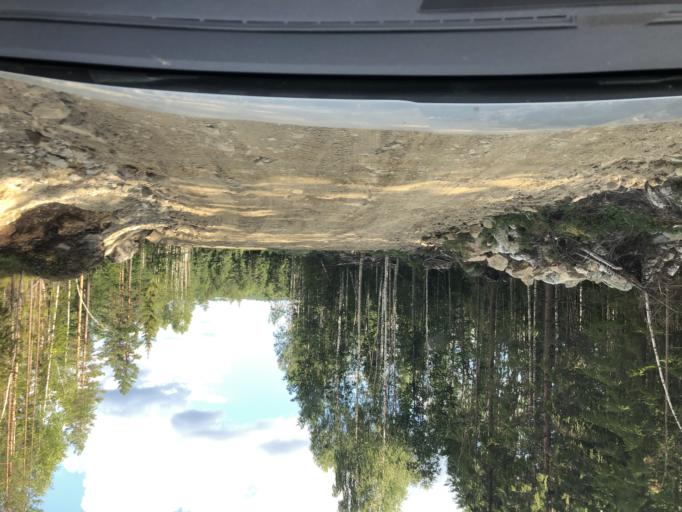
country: SE
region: Vaesternorrland
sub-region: Solleftea Kommun
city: Solleftea
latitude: 63.3121
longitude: 17.2806
